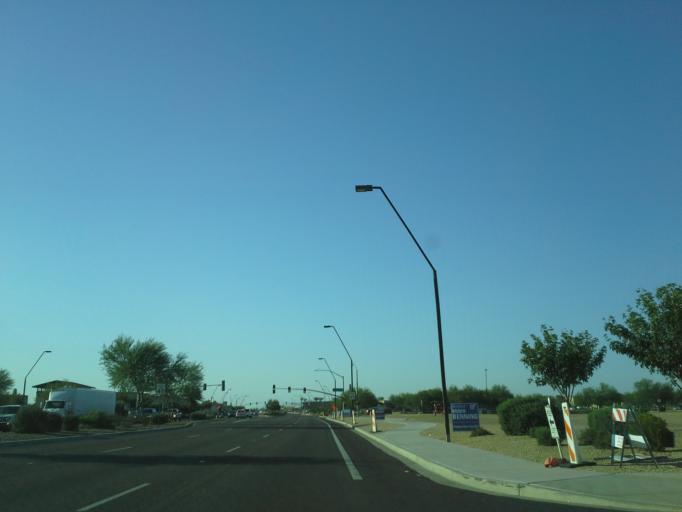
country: US
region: Arizona
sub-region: Maricopa County
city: Queen Creek
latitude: 33.2502
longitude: -111.6377
